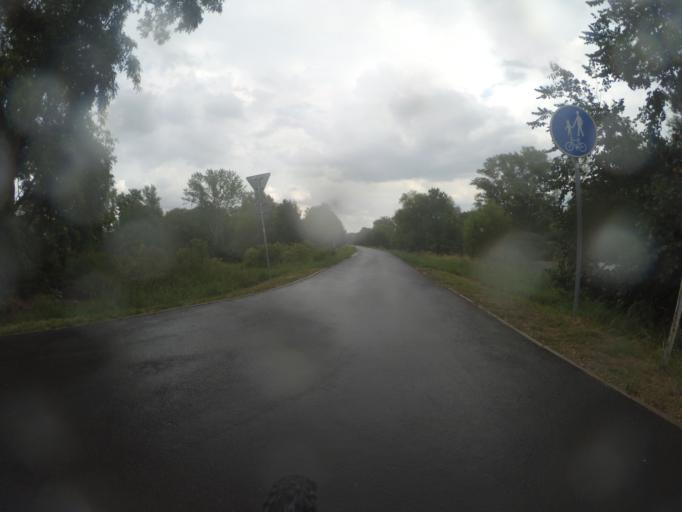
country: CZ
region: Central Bohemia
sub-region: Okres Melnik
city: Melnik
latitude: 50.3233
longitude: 14.4594
